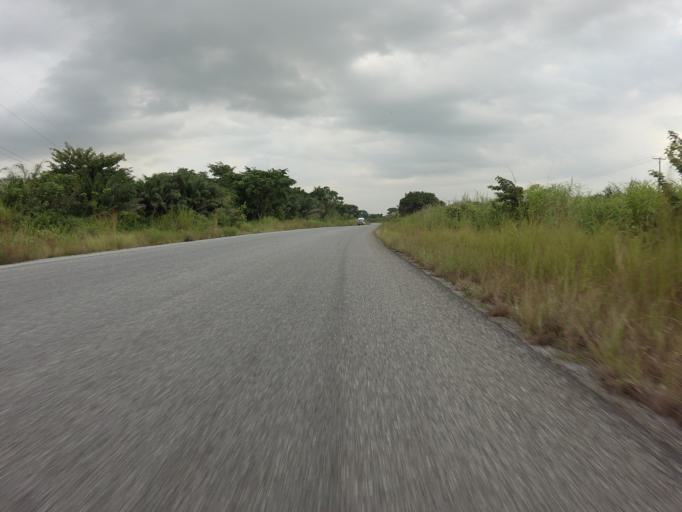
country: GH
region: Volta
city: Ho
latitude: 6.4775
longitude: 0.4959
